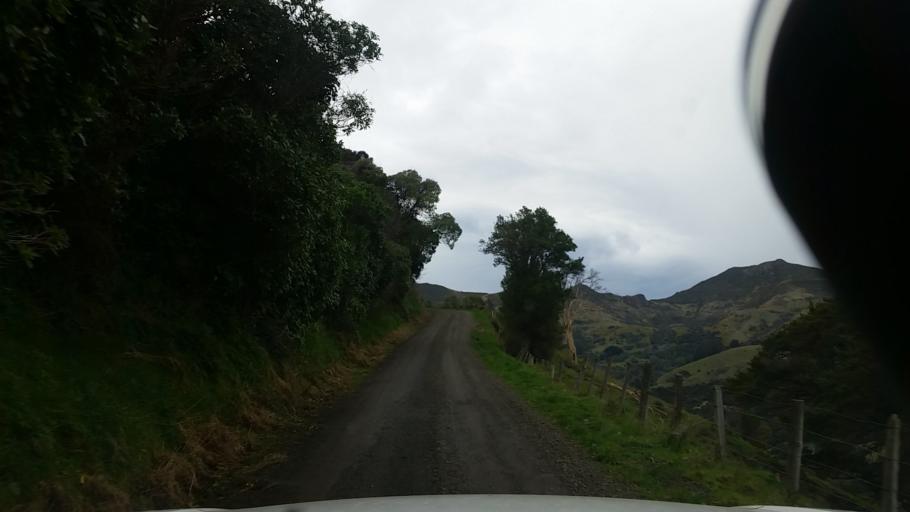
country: NZ
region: Canterbury
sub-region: Christchurch City
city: Christchurch
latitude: -43.7971
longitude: 172.9748
